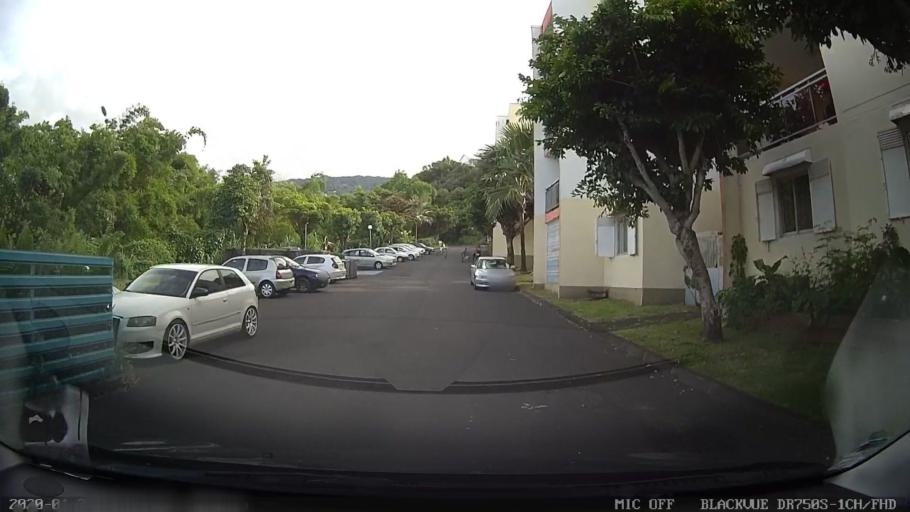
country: RE
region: Reunion
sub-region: Reunion
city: Sainte-Marie
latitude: -20.9279
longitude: 55.5275
